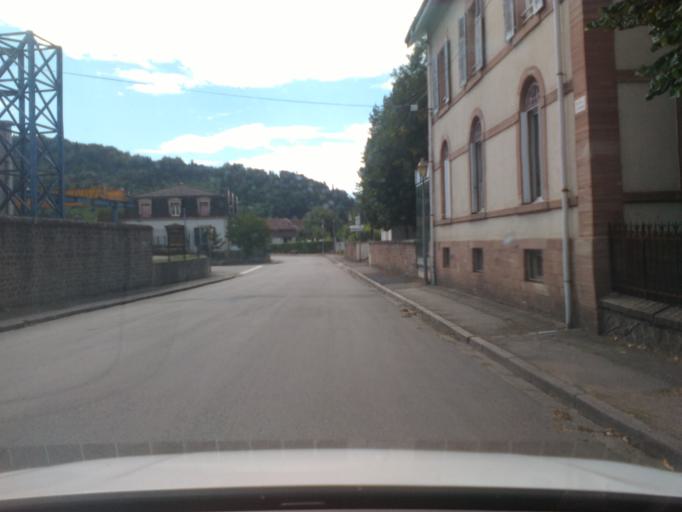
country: FR
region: Lorraine
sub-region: Departement des Vosges
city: Senones
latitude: 48.3936
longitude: 6.9780
